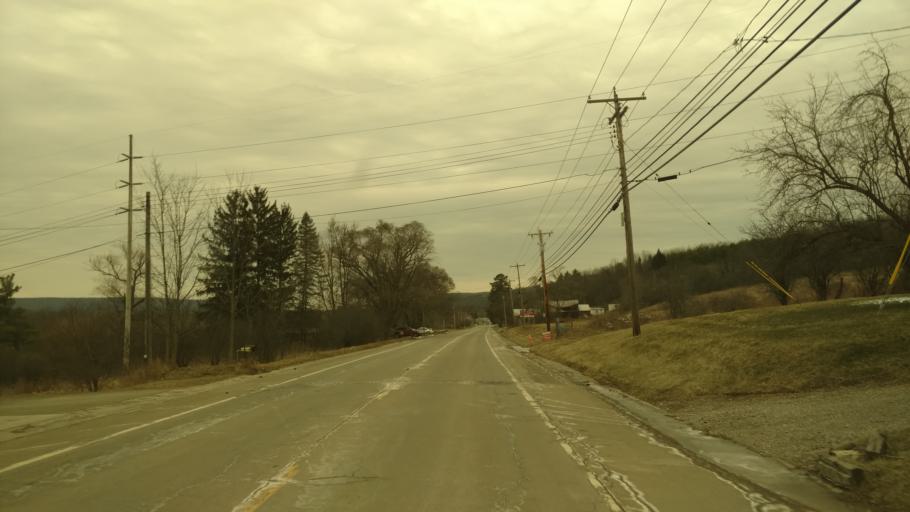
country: US
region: New York
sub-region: Allegany County
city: Wellsville
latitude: 42.1045
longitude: -77.9281
